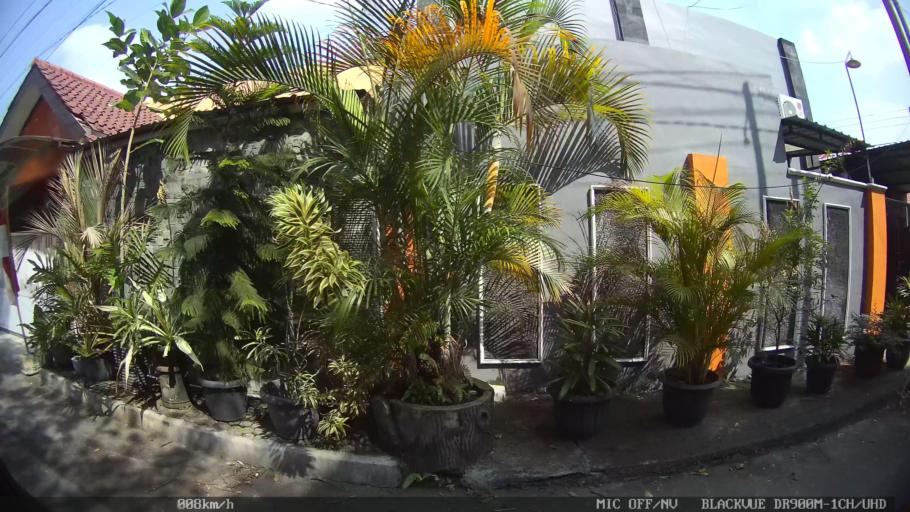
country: ID
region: Daerah Istimewa Yogyakarta
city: Yogyakarta
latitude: -7.8064
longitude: 110.3805
